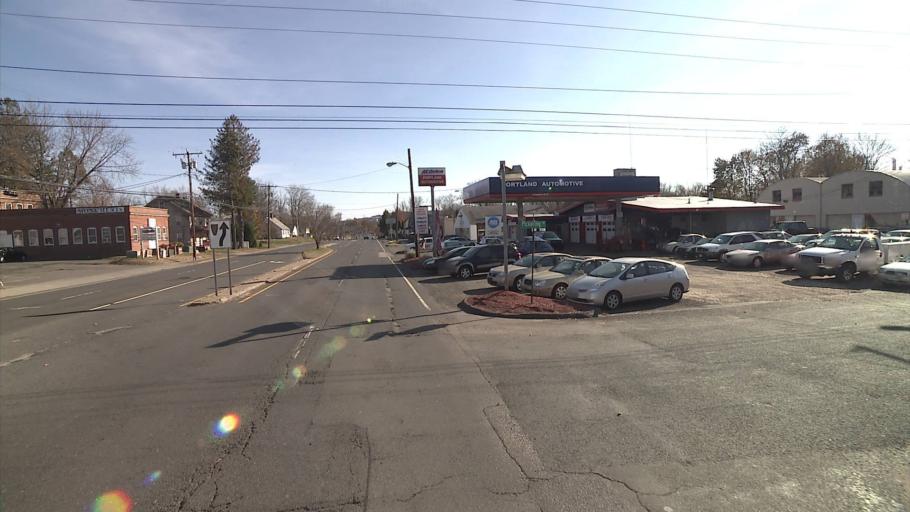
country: US
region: Connecticut
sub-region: Middlesex County
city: Portland
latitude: 41.5710
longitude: -72.6356
